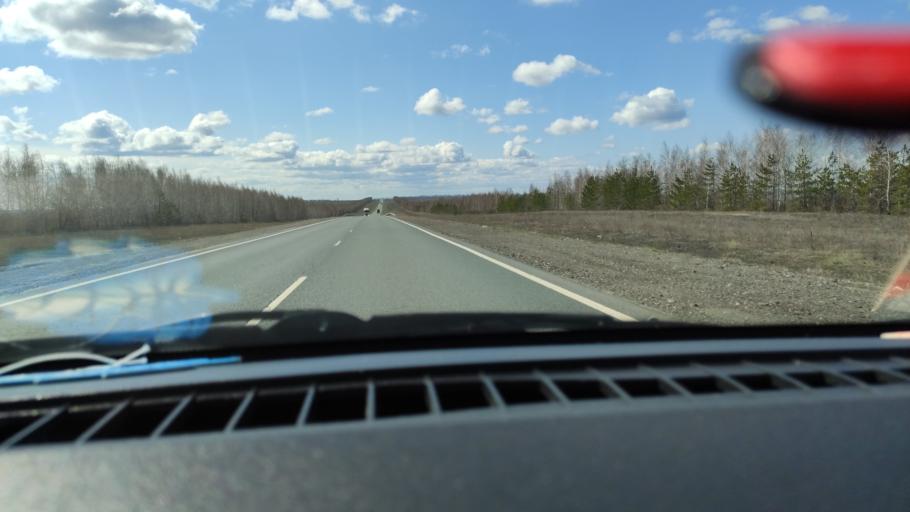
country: RU
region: Saratov
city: Dukhovnitskoye
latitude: 52.8284
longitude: 48.2380
